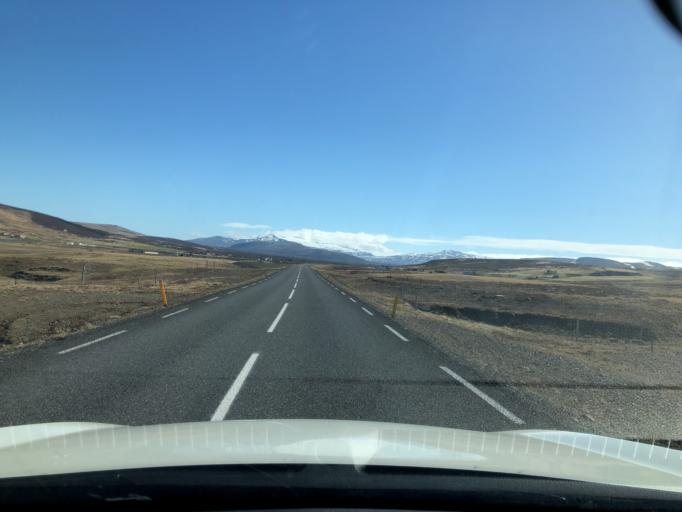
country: IS
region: South
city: Hveragerdi
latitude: 64.6988
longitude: -21.0634
